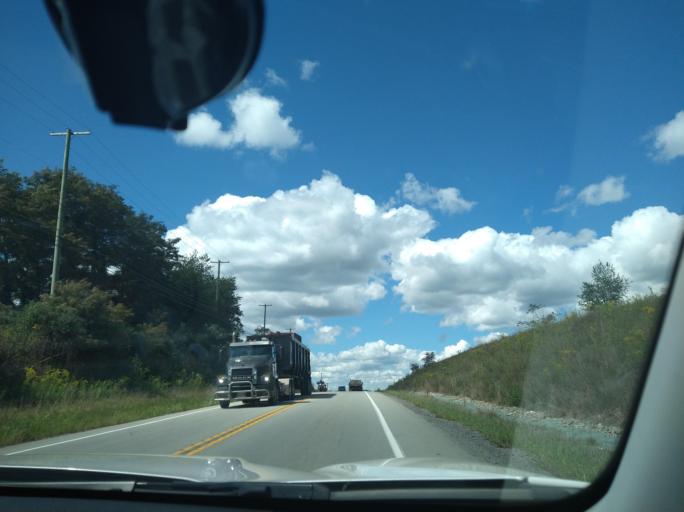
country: US
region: Pennsylvania
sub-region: Fayette County
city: Bear Rocks
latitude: 40.1017
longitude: -79.3661
